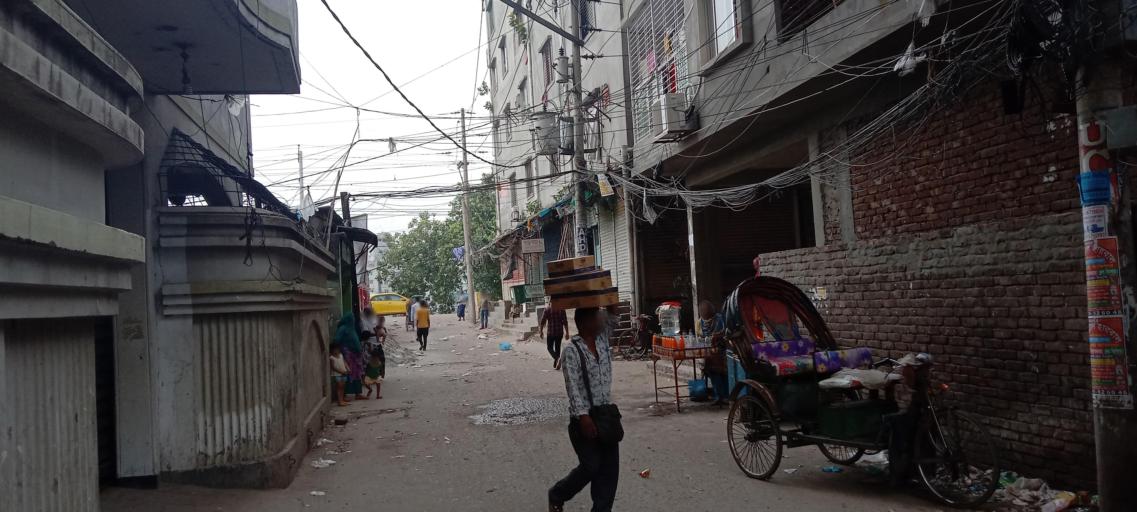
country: BD
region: Dhaka
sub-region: Dhaka
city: Dhaka
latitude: 23.7061
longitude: 90.4029
